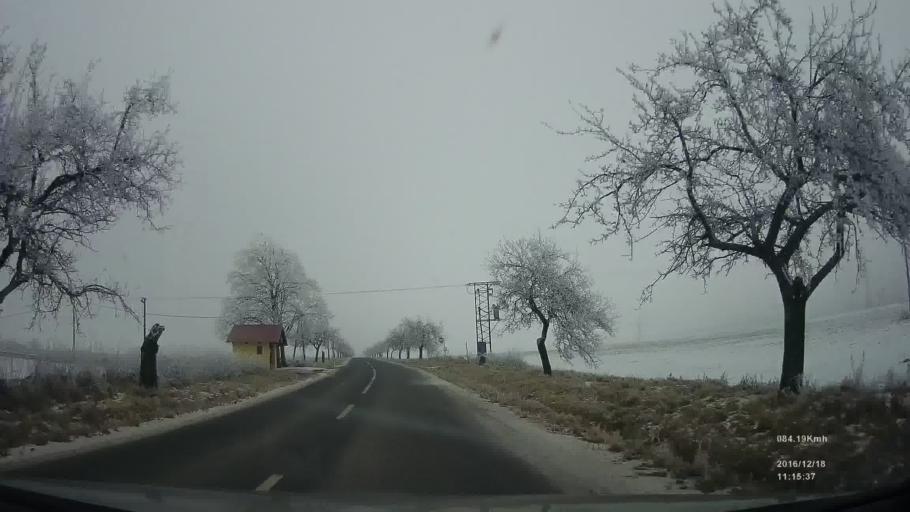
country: SK
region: Presovsky
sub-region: Okres Presov
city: Presov
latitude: 48.9074
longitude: 21.3246
